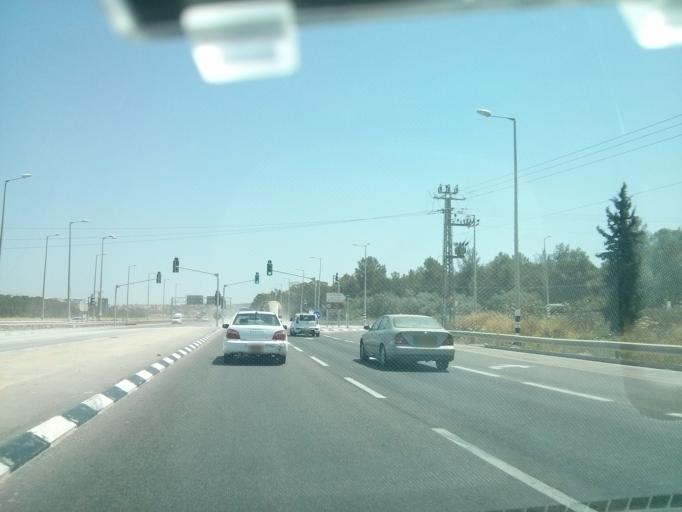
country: PS
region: West Bank
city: Barta`ah ash Sharqiyah
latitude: 32.4852
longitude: 35.0449
